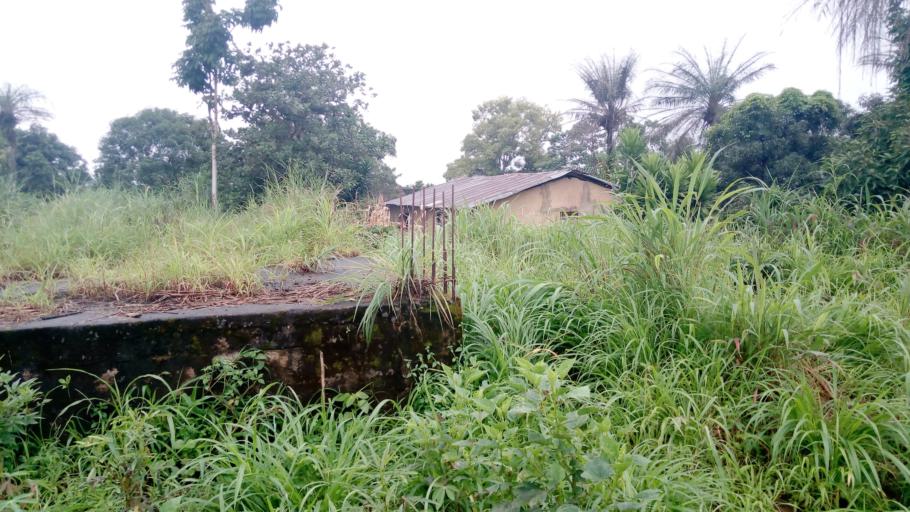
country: SL
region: Western Area
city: Waterloo
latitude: 8.3388
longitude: -12.9928
